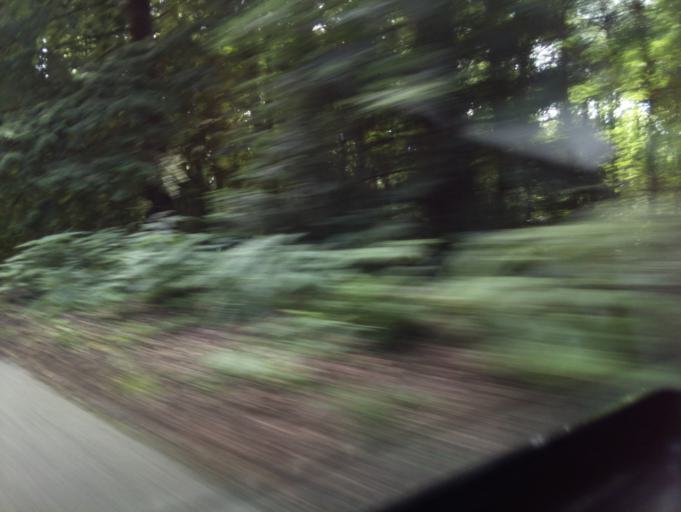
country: GB
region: England
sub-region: Gloucestershire
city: Cinderford
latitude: 51.7954
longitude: -2.4957
